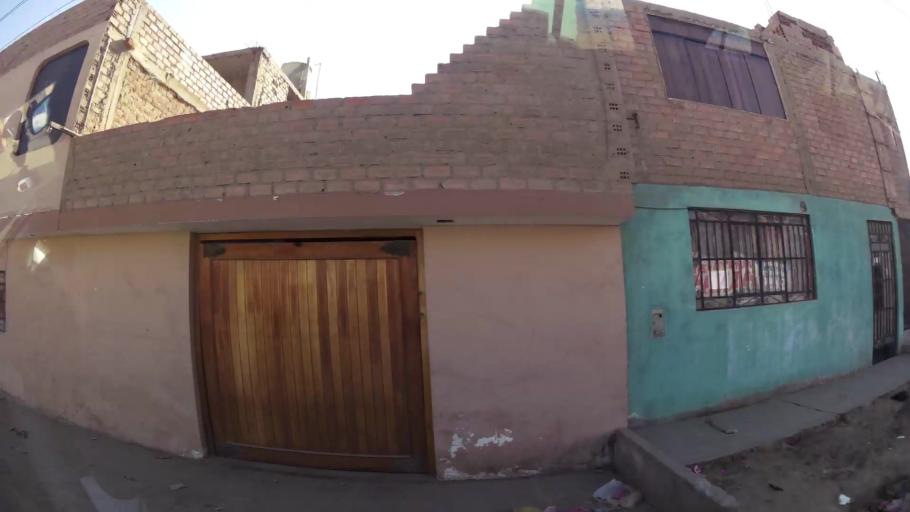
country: PE
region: Ica
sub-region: Provincia de Chincha
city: Chincha Alta
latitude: -13.4125
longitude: -76.1388
